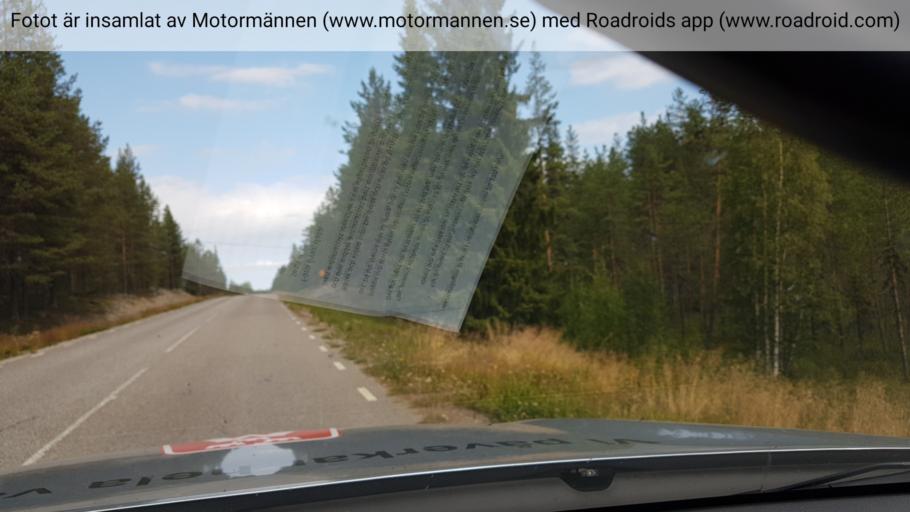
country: SE
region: Vaesterbotten
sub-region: Skelleftea Kommun
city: Boliden
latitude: 65.2924
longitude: 20.2210
